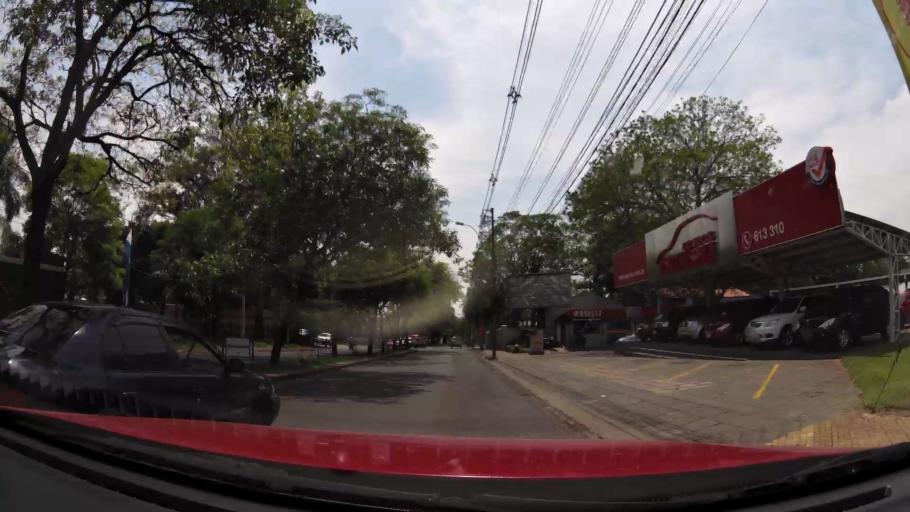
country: PY
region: Central
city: Lambare
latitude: -25.3009
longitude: -57.5804
